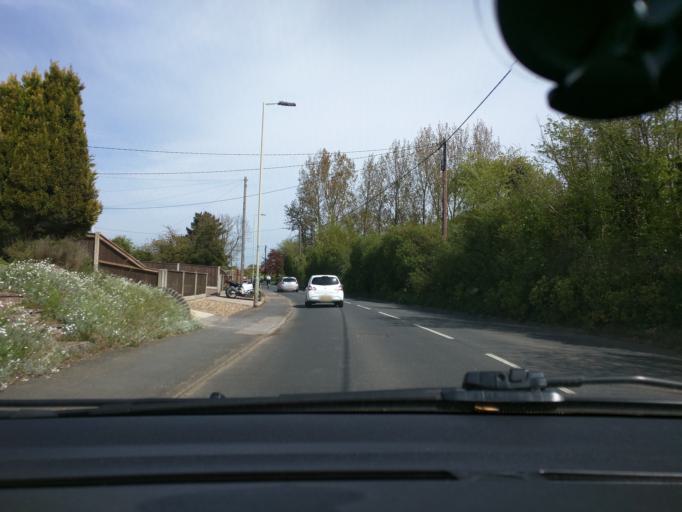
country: GB
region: England
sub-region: Suffolk
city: Leiston
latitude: 52.2153
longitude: 1.5778
